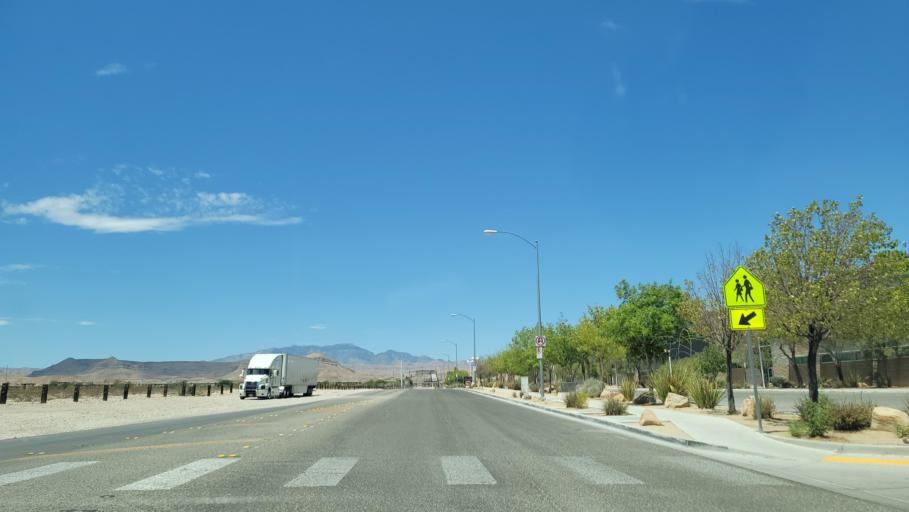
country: US
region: Nevada
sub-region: Clark County
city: Enterprise
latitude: 35.9914
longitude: -115.2359
